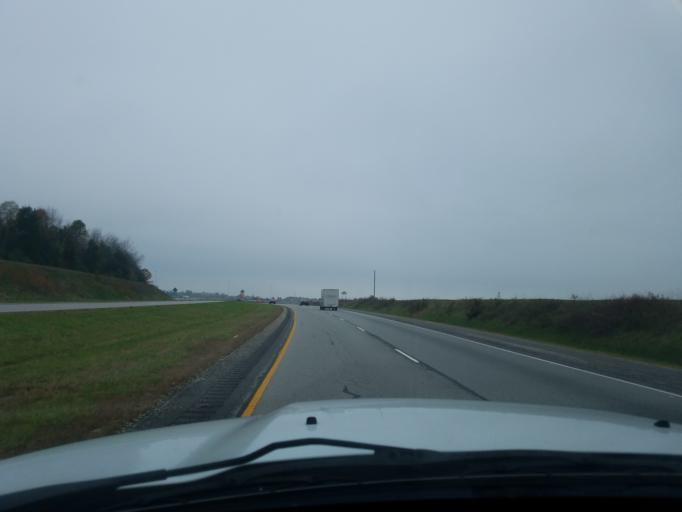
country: US
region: Kentucky
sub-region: Hardin County
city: Elizabethtown
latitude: 37.6669
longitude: -85.8407
